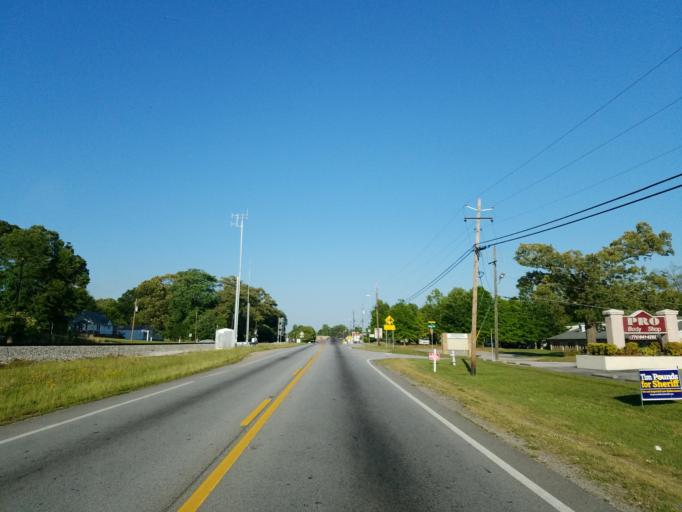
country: US
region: Georgia
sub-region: Douglas County
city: Lithia Springs
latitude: 33.7936
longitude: -84.6665
